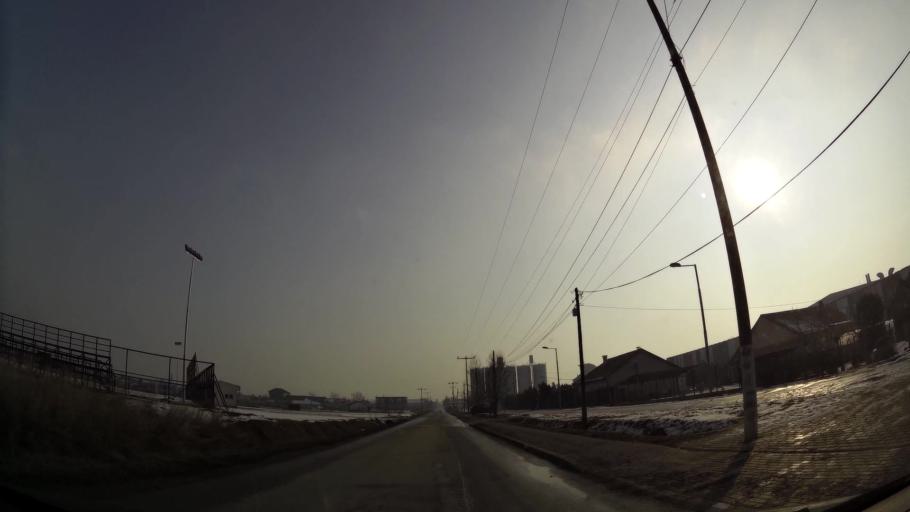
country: MK
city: Kadino
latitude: 41.9766
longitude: 21.5940
